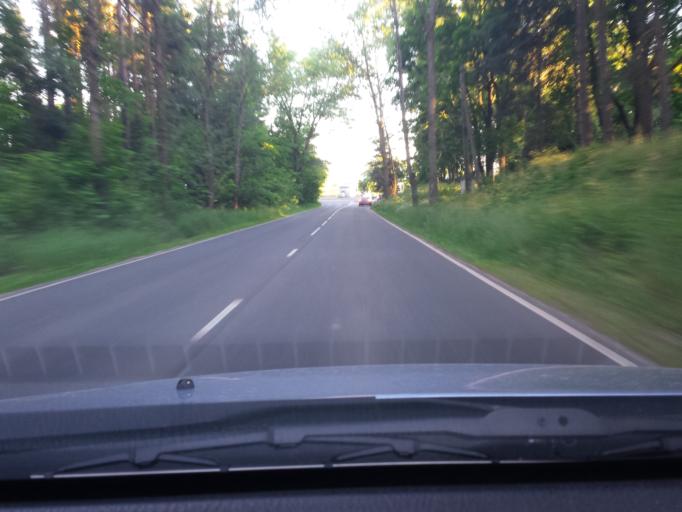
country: LV
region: Riga
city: Jaunciems
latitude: 57.0541
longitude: 24.1555
